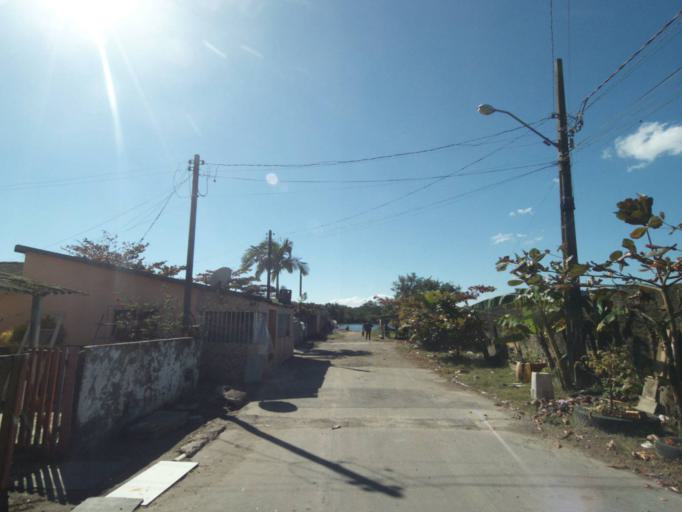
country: BR
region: Parana
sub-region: Paranagua
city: Paranagua
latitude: -25.5123
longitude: -48.4991
